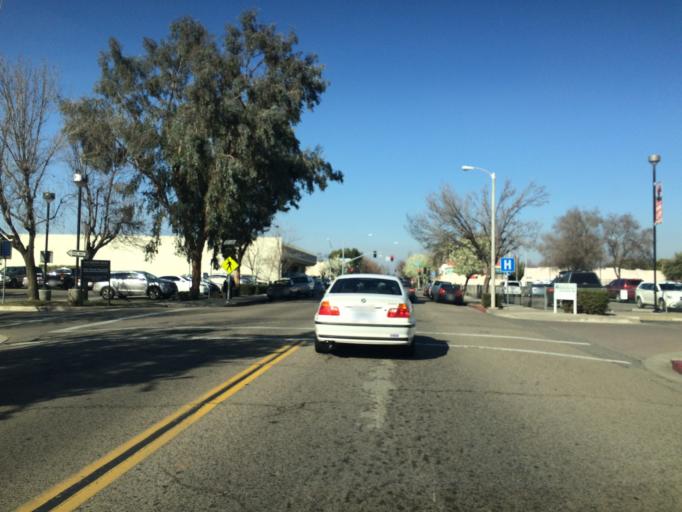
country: US
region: California
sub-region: Tulare County
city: Visalia
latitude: 36.3281
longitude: -119.2965
